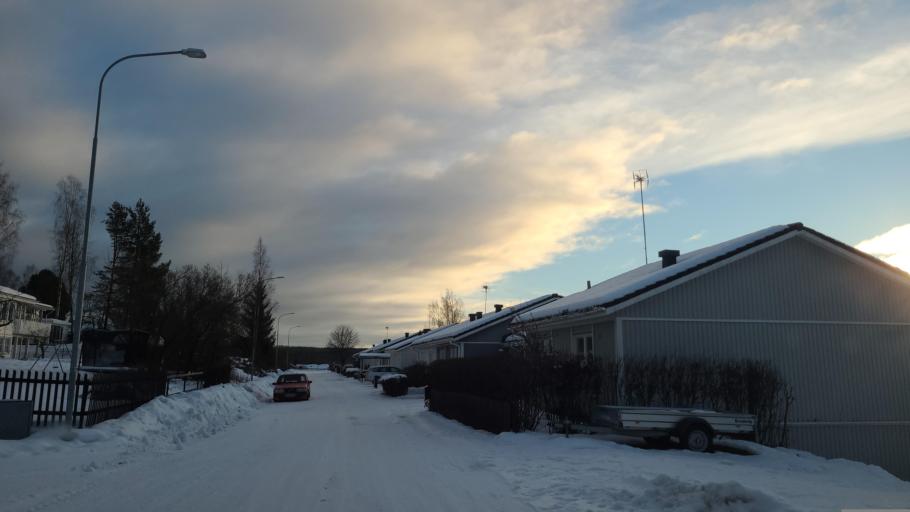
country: SE
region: Gaevleborg
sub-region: Bollnas Kommun
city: Bollnas
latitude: 61.3598
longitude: 16.4170
